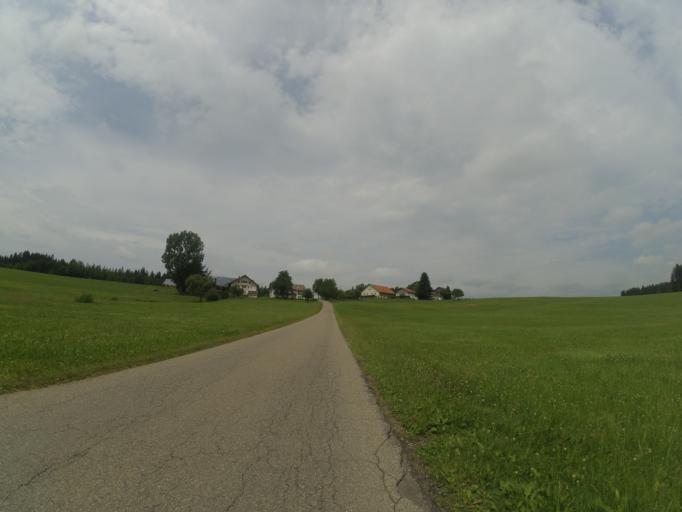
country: DE
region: Baden-Wuerttemberg
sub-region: Tuebingen Region
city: Leutkirch im Allgau
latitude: 47.7564
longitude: 9.9989
